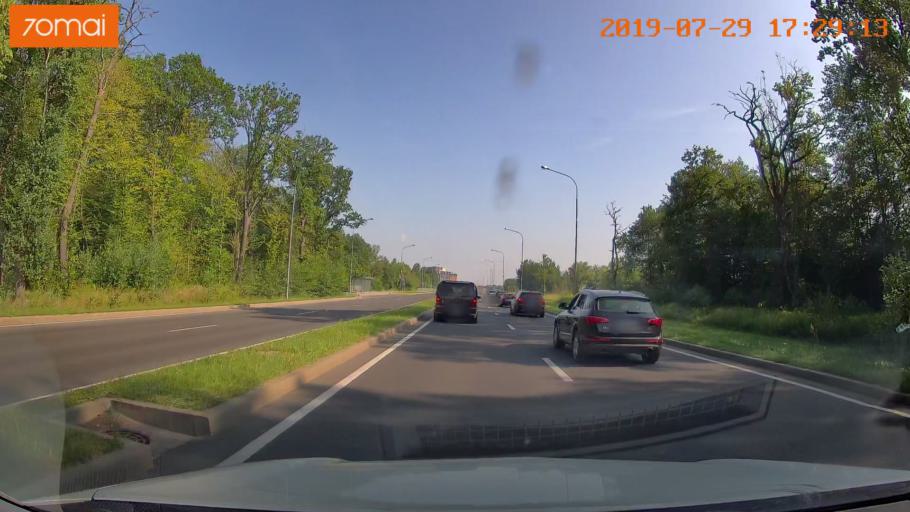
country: RU
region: Kaliningrad
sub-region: Gorod Kaliningrad
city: Kaliningrad
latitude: 54.7566
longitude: 20.4720
